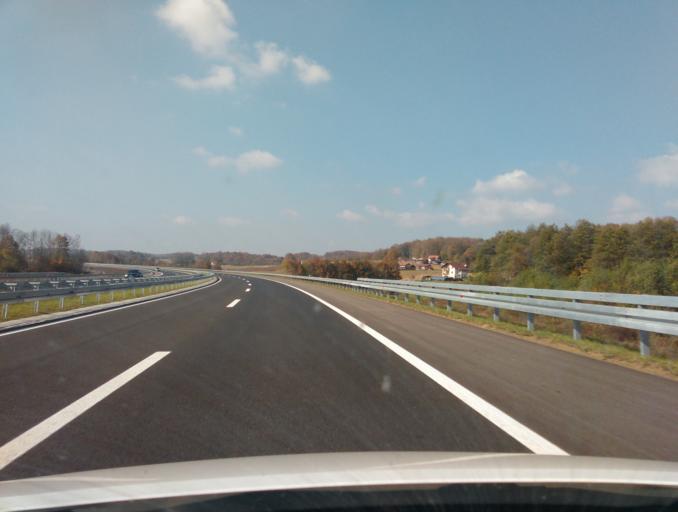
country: BA
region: Republika Srpska
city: Prnjavor
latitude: 44.8943
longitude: 17.6022
